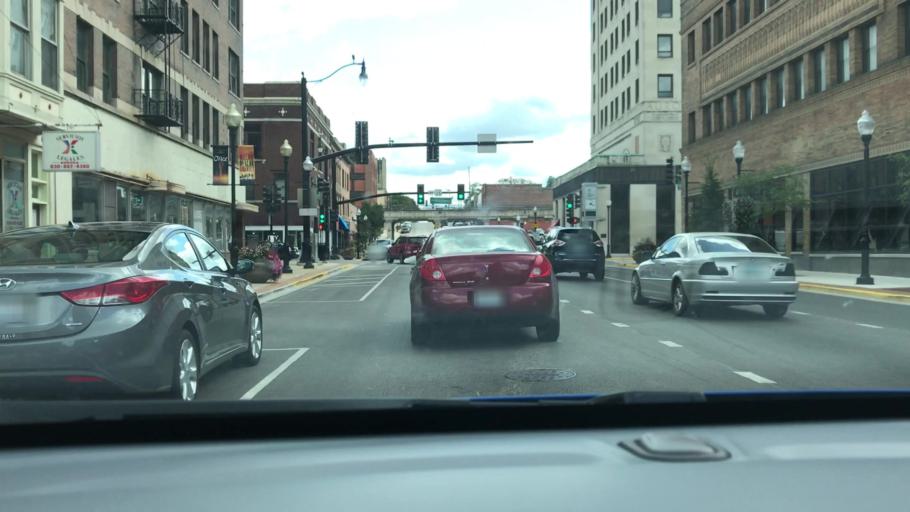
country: US
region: Illinois
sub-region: Kane County
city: Aurora
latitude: 41.7574
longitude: -88.3135
